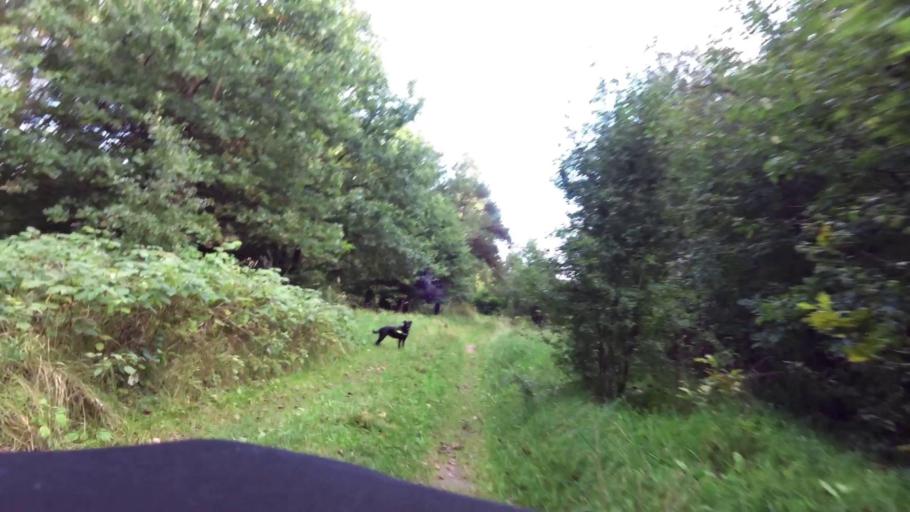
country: PL
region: West Pomeranian Voivodeship
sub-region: Powiat stargardzki
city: Marianowo
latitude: 53.3836
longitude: 15.3449
